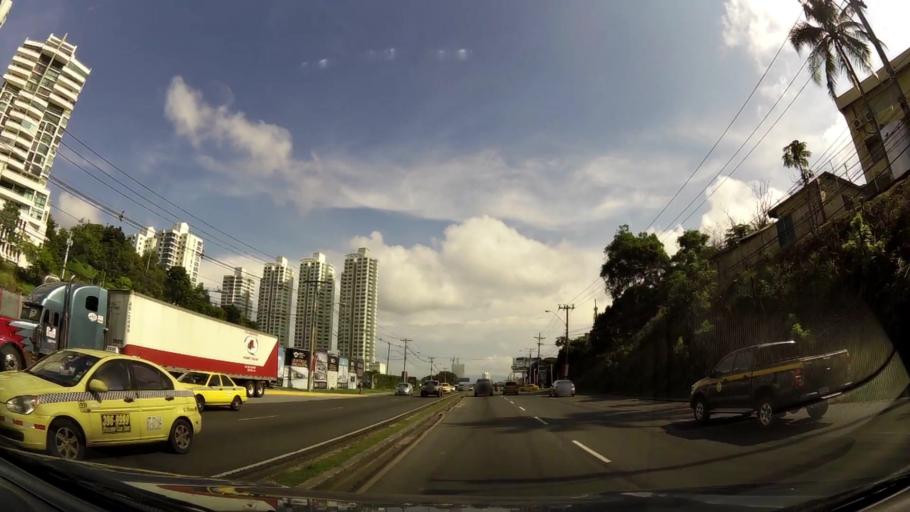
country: PA
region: Panama
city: Panama
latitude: 8.9918
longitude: -79.5307
